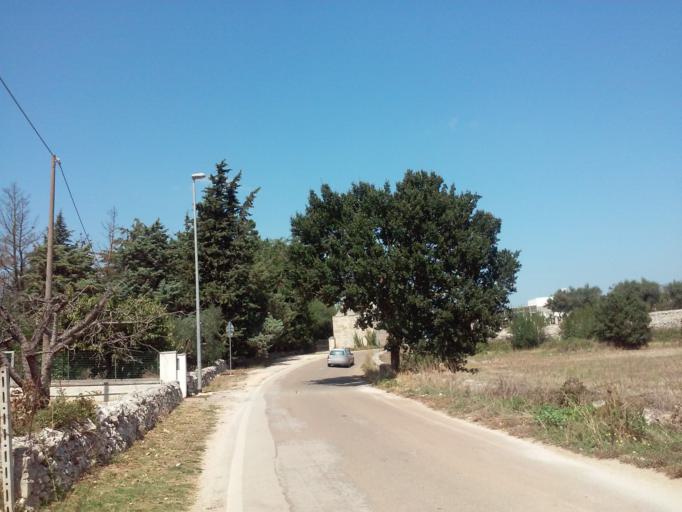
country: IT
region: Apulia
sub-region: Provincia di Bari
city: Alberobello
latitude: 40.7934
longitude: 17.2214
